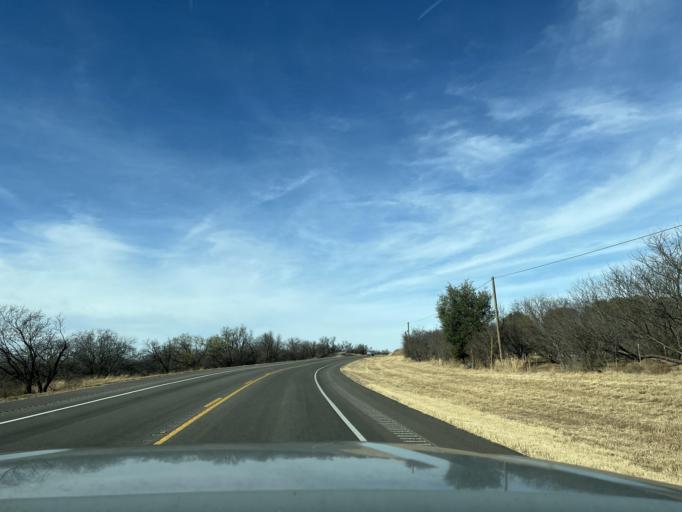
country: US
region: Texas
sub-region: Shackelford County
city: Albany
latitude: 32.5779
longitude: -99.1820
